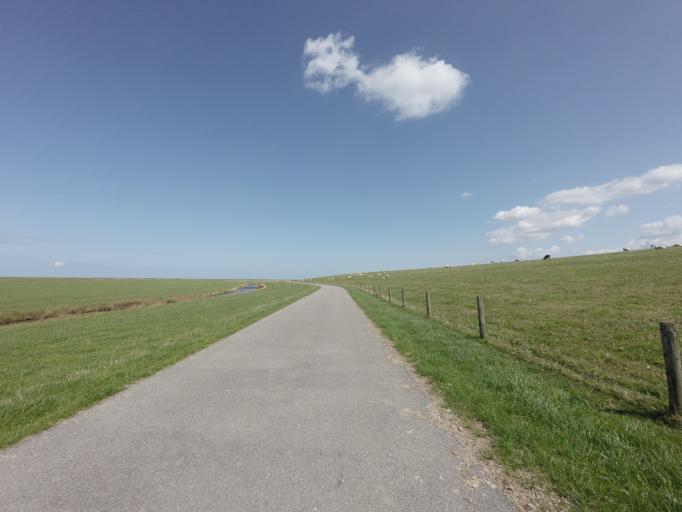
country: NL
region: Friesland
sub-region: Gemeente Ferwerderadiel
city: Marrum
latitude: 53.3353
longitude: 5.7815
